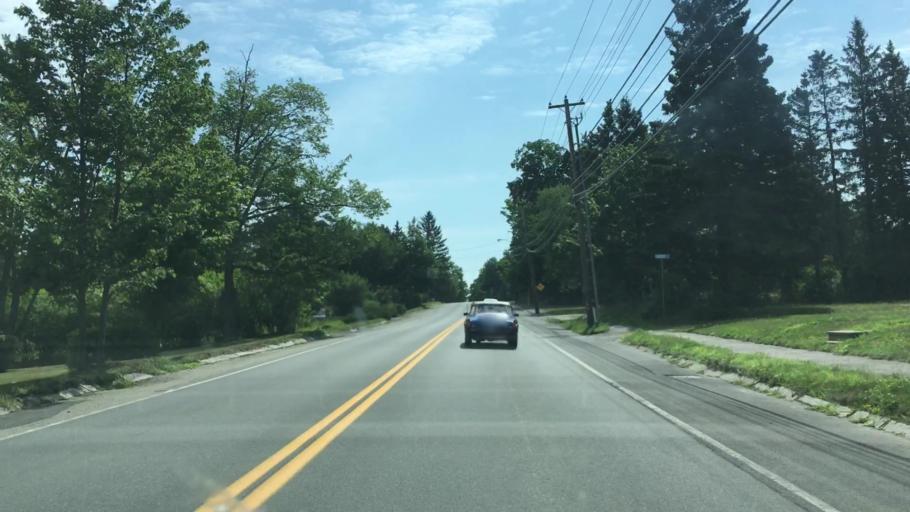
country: US
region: Maine
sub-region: Washington County
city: Calais
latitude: 45.1827
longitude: -67.2634
